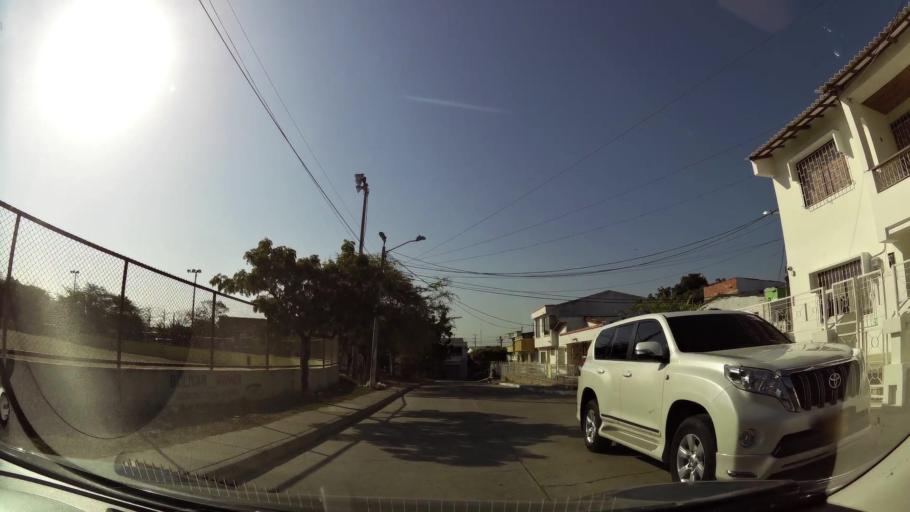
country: CO
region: Bolivar
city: Cartagena
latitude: 10.3915
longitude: -75.5058
